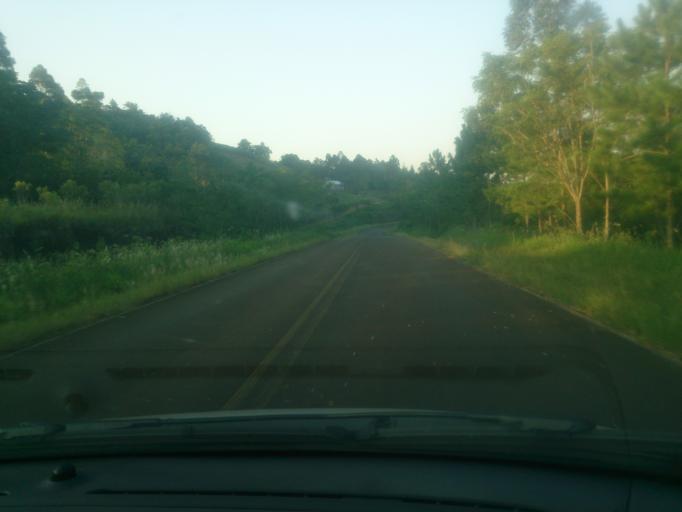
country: AR
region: Misiones
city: Panambi
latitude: -27.6617
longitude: -54.9103
